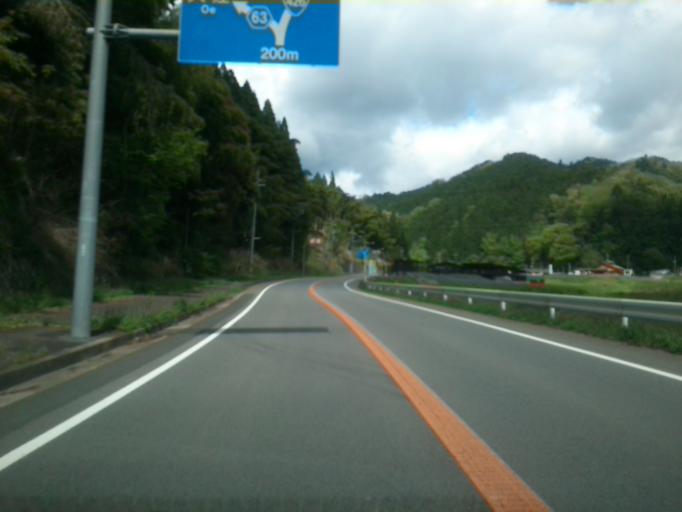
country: JP
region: Kyoto
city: Fukuchiyama
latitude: 35.4215
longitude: 135.0244
